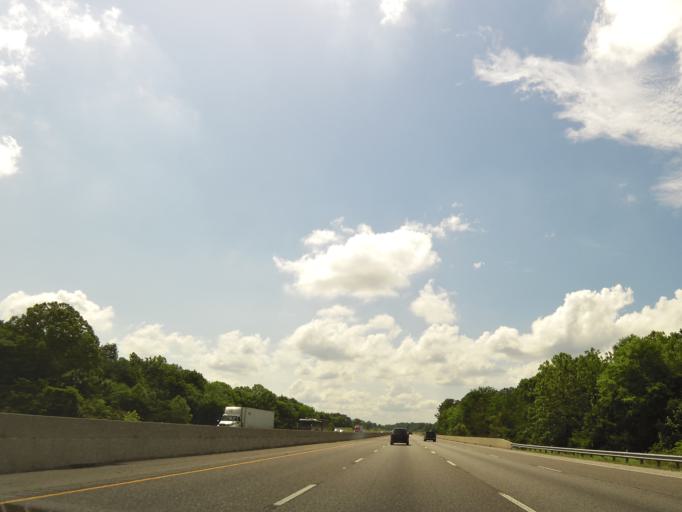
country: US
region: Alabama
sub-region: Calhoun County
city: Bynum
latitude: 33.5826
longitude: -86.0276
